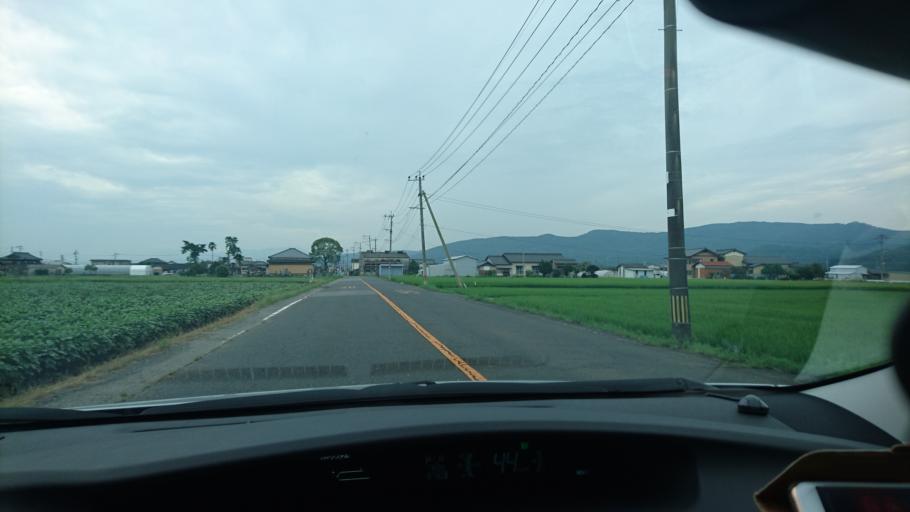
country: JP
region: Saga Prefecture
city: Takeocho-takeo
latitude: 33.1977
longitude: 130.1150
